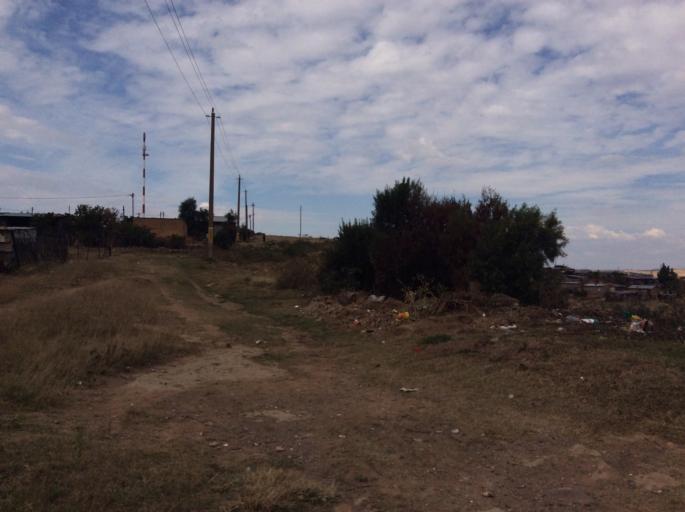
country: LS
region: Mafeteng
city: Mafeteng
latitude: -29.7215
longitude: 27.0281
